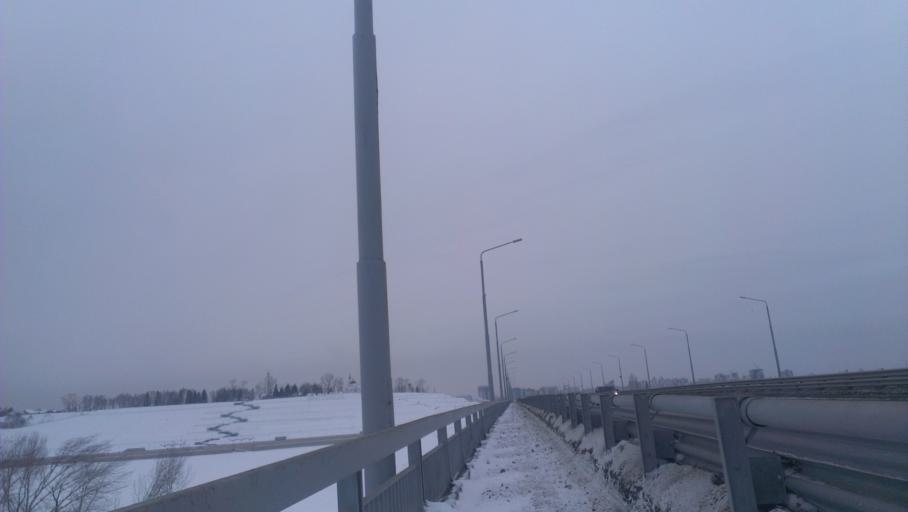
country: RU
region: Altai Krai
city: Zaton
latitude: 53.3214
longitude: 83.8090
